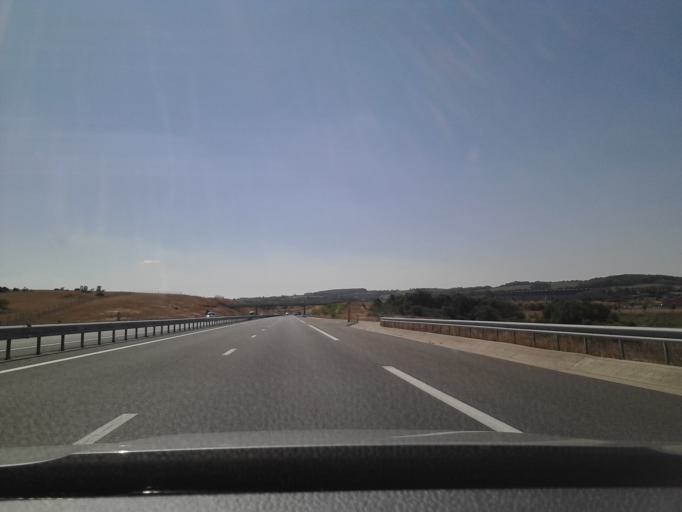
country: FR
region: Midi-Pyrenees
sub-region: Departement de l'Aveyron
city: La Cavalerie
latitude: 44.0188
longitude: 3.1296
